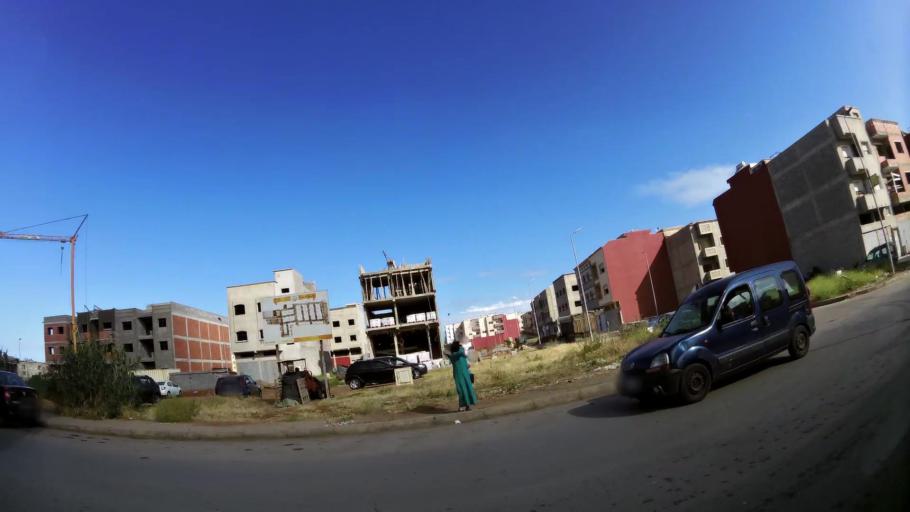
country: MA
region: Rabat-Sale-Zemmour-Zaer
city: Sale
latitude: 34.0582
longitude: -6.8078
